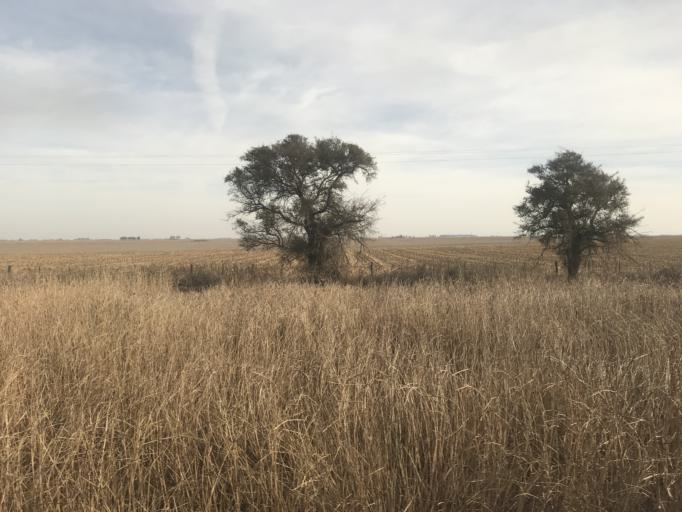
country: AR
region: Cordoba
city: Pilar
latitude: -31.7218
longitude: -63.8512
